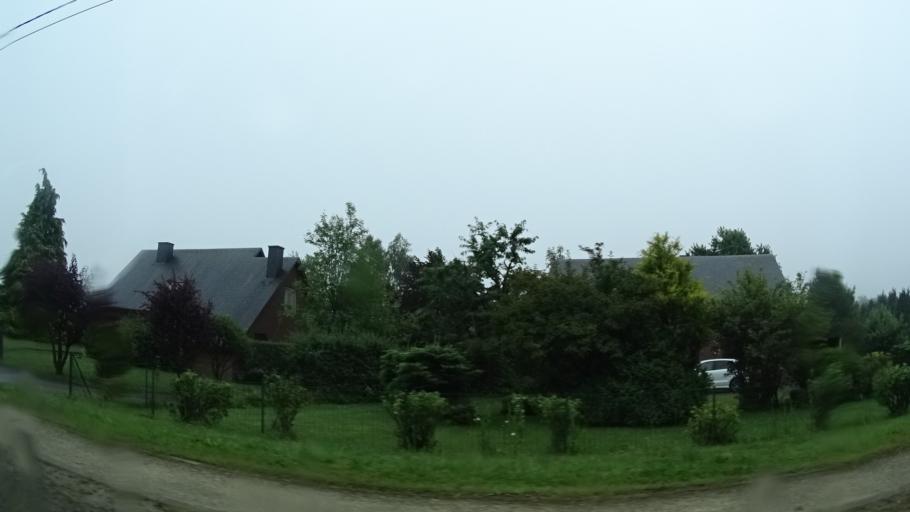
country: BE
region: Wallonia
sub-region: Province de Namur
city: Bievre
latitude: 50.0004
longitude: 5.0110
